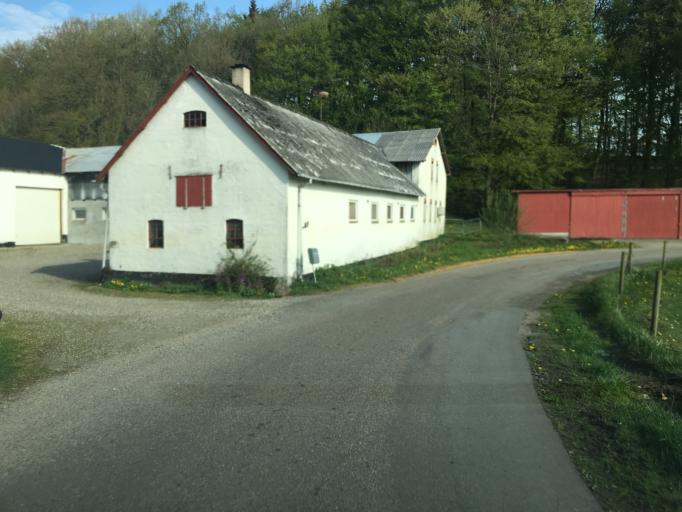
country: DK
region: South Denmark
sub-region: Haderslev Kommune
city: Vojens
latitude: 55.1881
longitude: 9.3868
